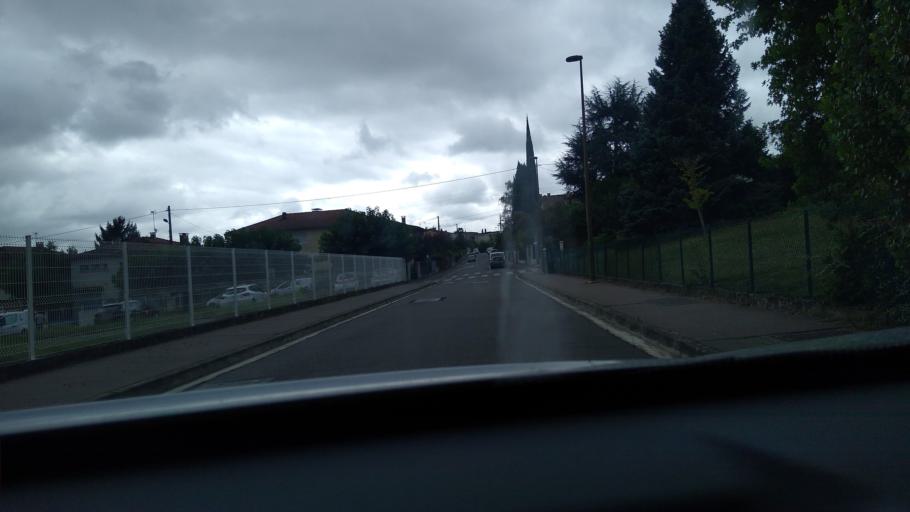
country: FR
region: Midi-Pyrenees
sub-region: Departement de la Haute-Garonne
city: Balma
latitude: 43.6107
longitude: 1.4720
